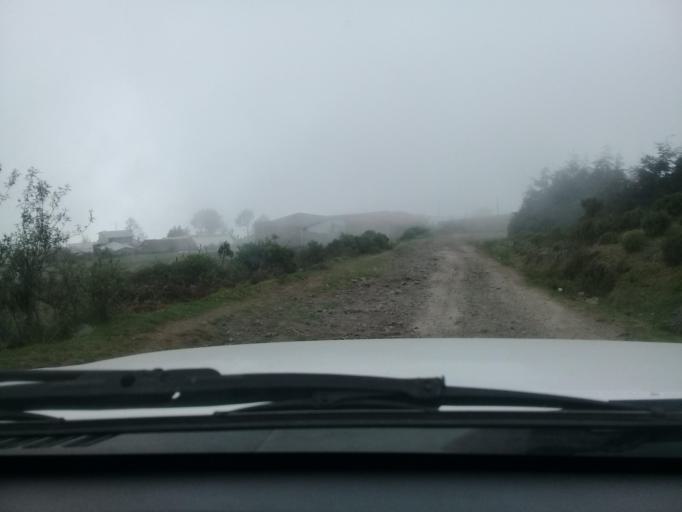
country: MX
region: Veracruz
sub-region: Mariano Escobedo
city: Texmola
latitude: 18.9598
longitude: -97.2188
